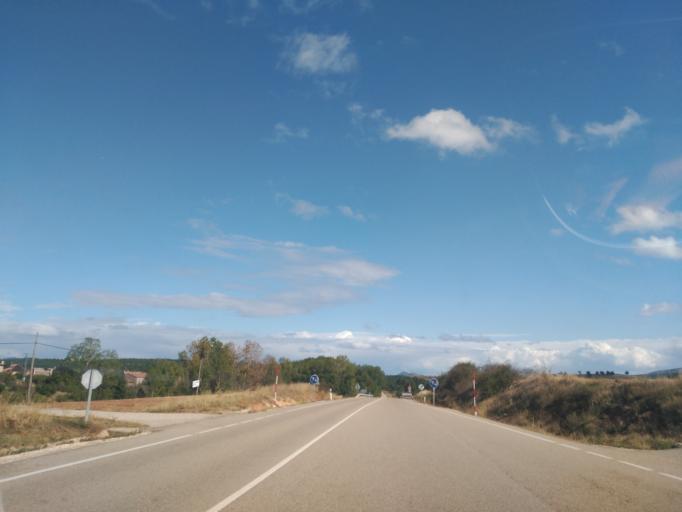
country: ES
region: Castille and Leon
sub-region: Provincia de Burgos
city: Pinilla de los Barruecos
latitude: 41.8983
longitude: -3.2686
